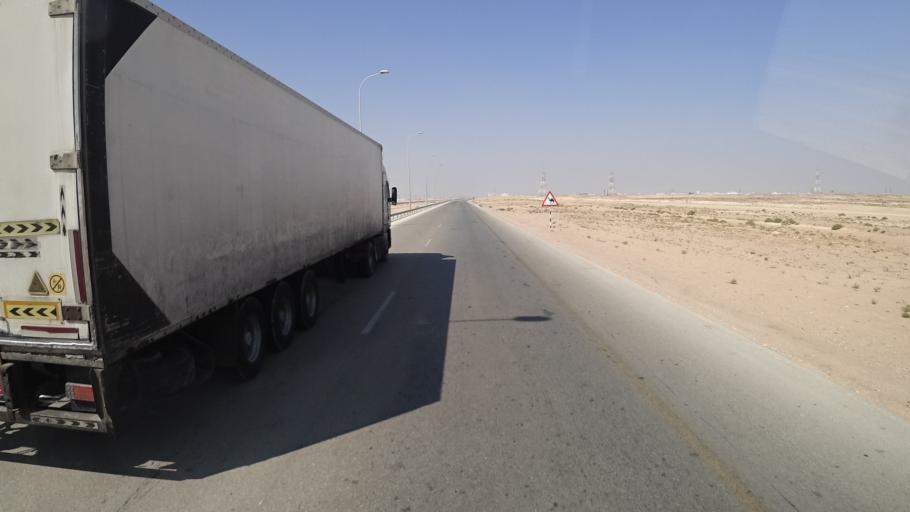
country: OM
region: Zufar
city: Salalah
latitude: 17.5833
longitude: 54.0423
